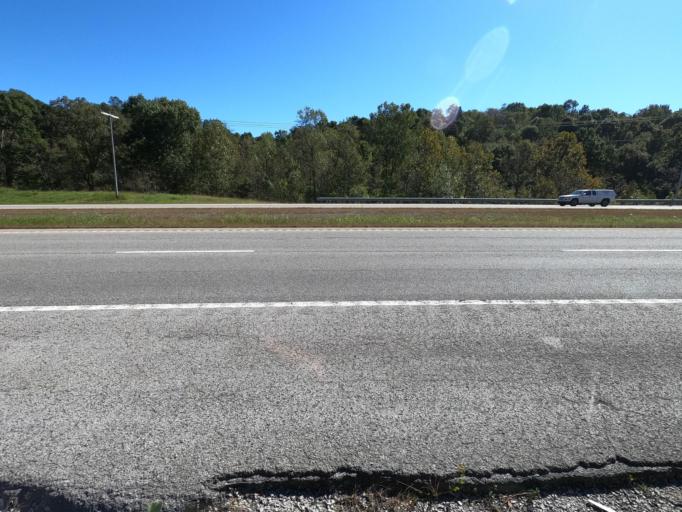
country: US
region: Tennessee
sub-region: Maury County
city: Mount Pleasant
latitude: 35.4783
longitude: -87.2596
